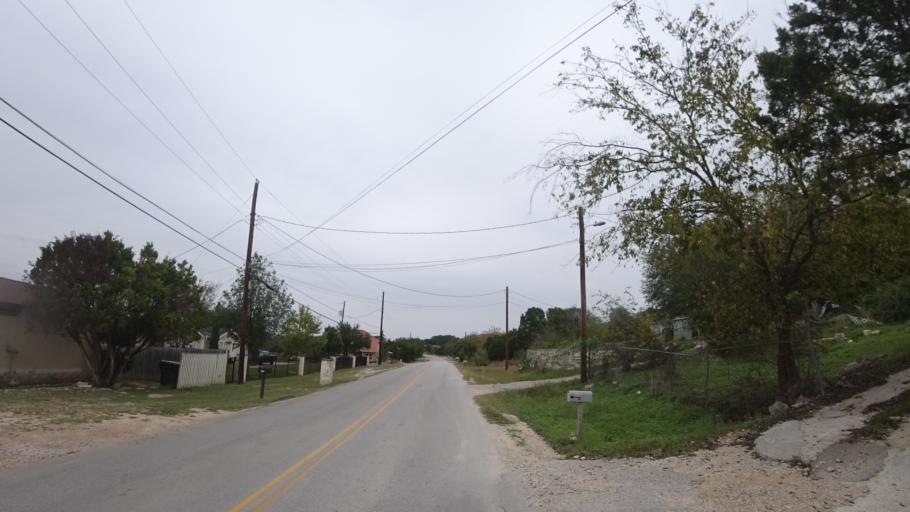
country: US
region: Texas
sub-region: Travis County
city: Lakeway
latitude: 30.3720
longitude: -97.9357
